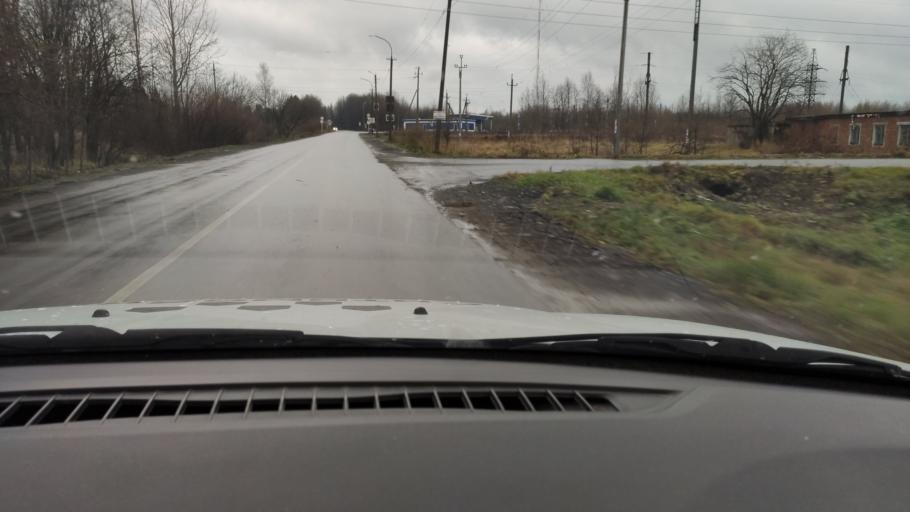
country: RU
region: Perm
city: Sylva
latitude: 58.0276
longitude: 56.7393
